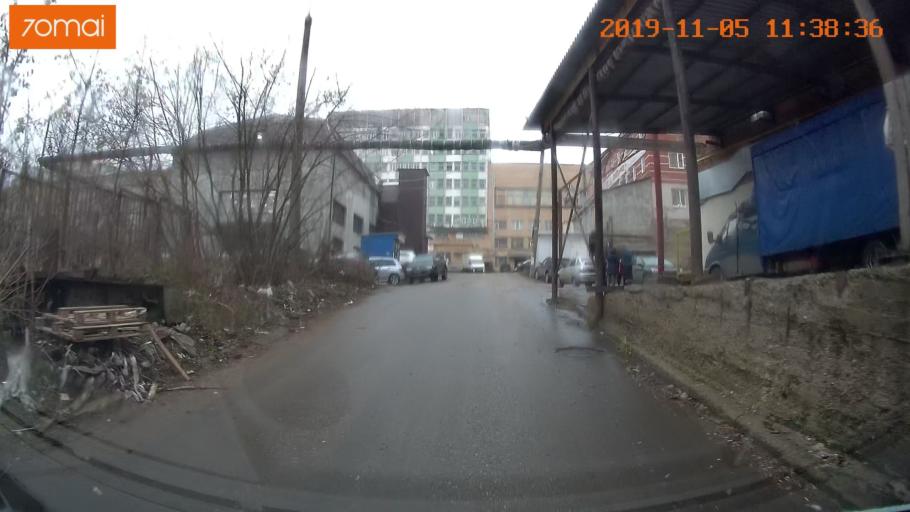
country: RU
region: Ivanovo
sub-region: Gorod Ivanovo
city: Ivanovo
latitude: 57.0102
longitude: 40.9583
